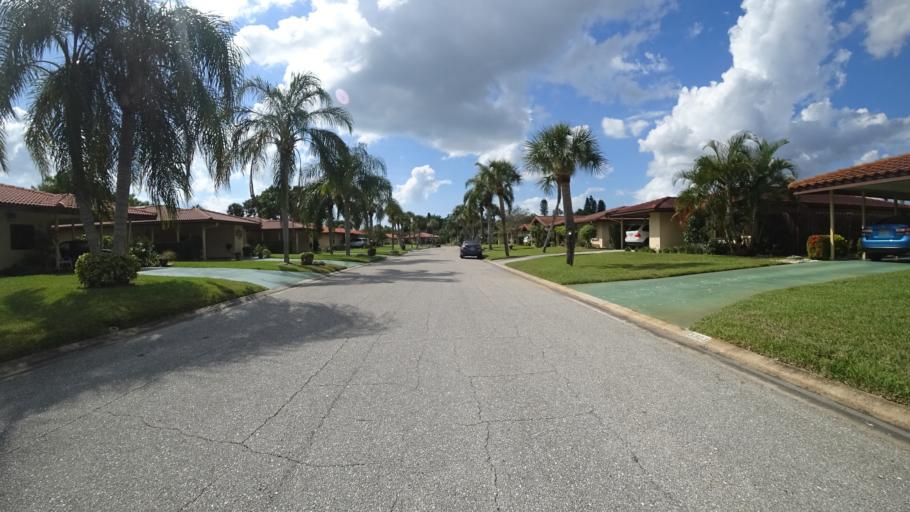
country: US
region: Florida
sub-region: Manatee County
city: Bayshore Gardens
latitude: 27.4274
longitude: -82.5942
